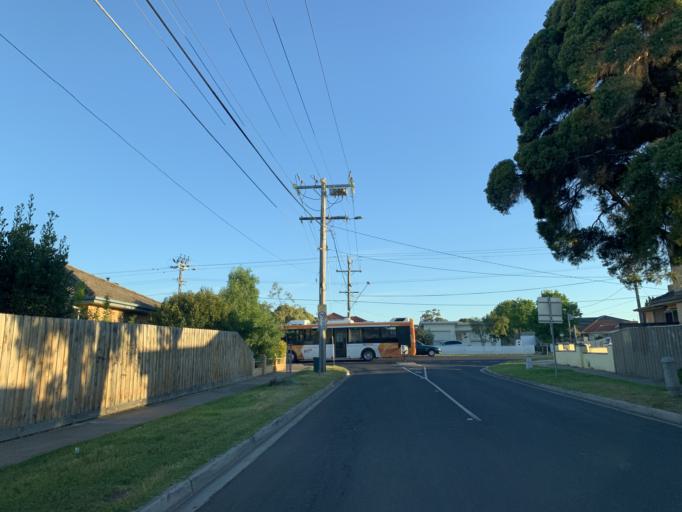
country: AU
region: Victoria
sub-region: Brimbank
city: St Albans
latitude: -37.7458
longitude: 144.8095
